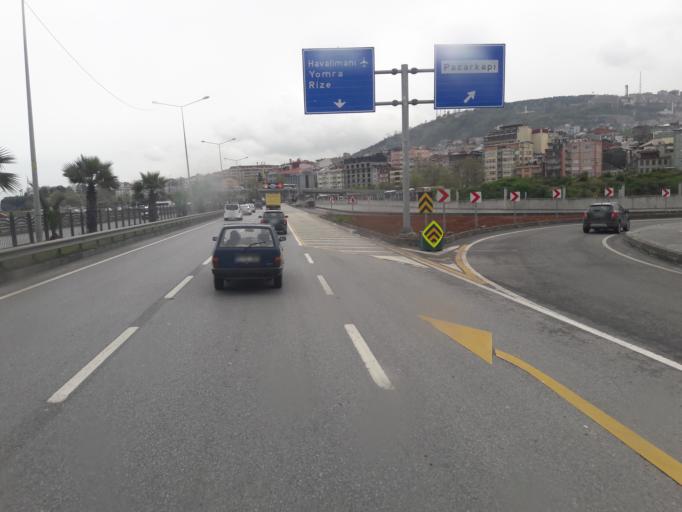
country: TR
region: Trabzon
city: Trabzon
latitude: 41.0109
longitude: 39.7241
